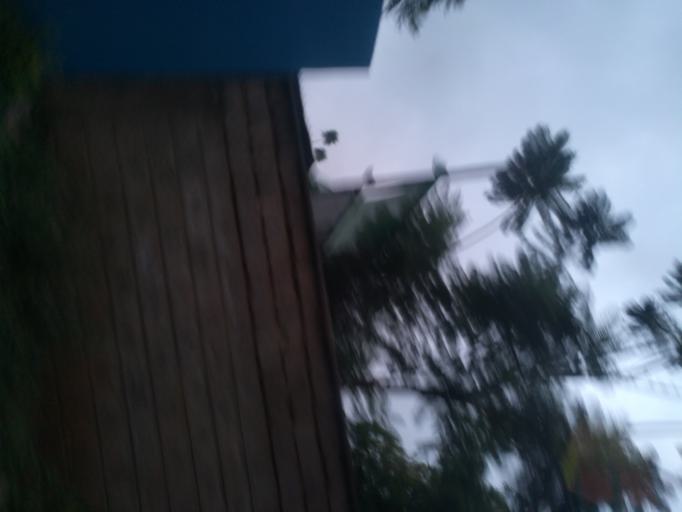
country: KE
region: Nairobi Area
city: Nairobi
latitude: -1.2947
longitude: 36.7952
